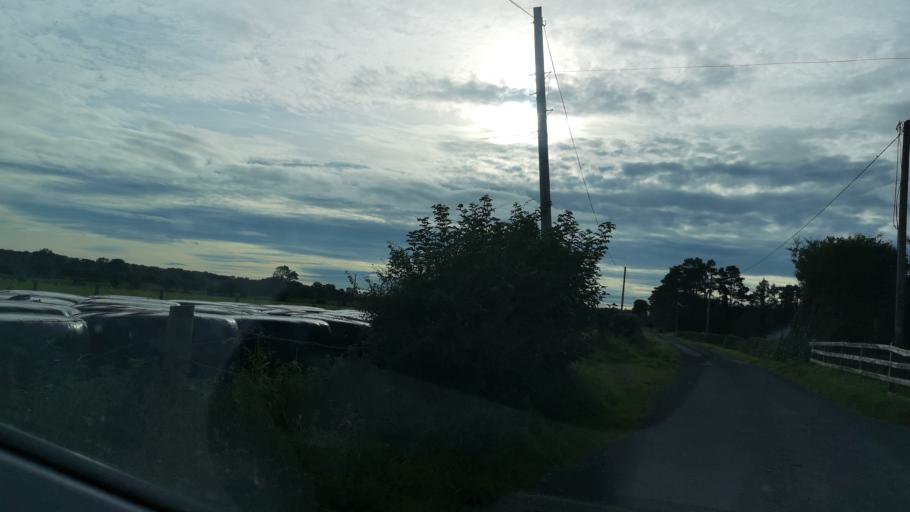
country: IE
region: Connaught
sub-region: County Galway
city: Ballinasloe
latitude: 53.3425
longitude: -8.2739
